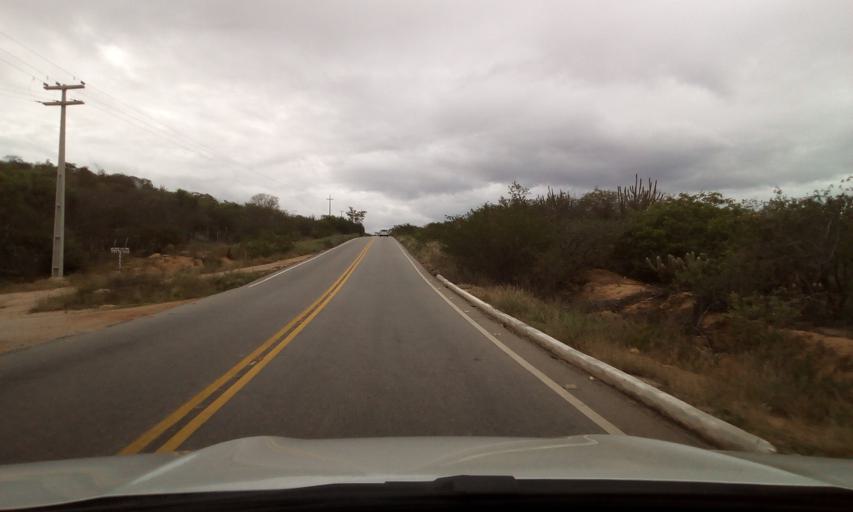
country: BR
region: Paraiba
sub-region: Picui
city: Picui
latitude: -6.5336
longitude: -36.3072
